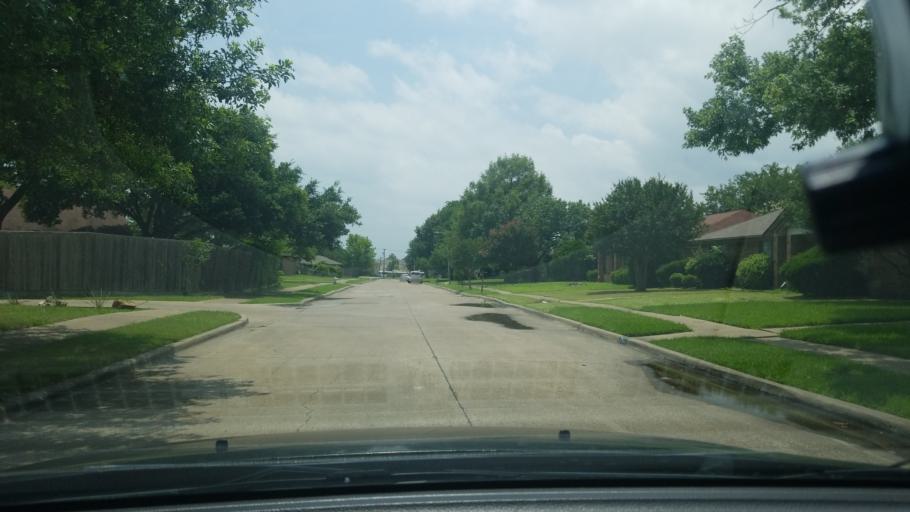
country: US
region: Texas
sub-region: Dallas County
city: Mesquite
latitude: 32.7983
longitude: -96.6145
